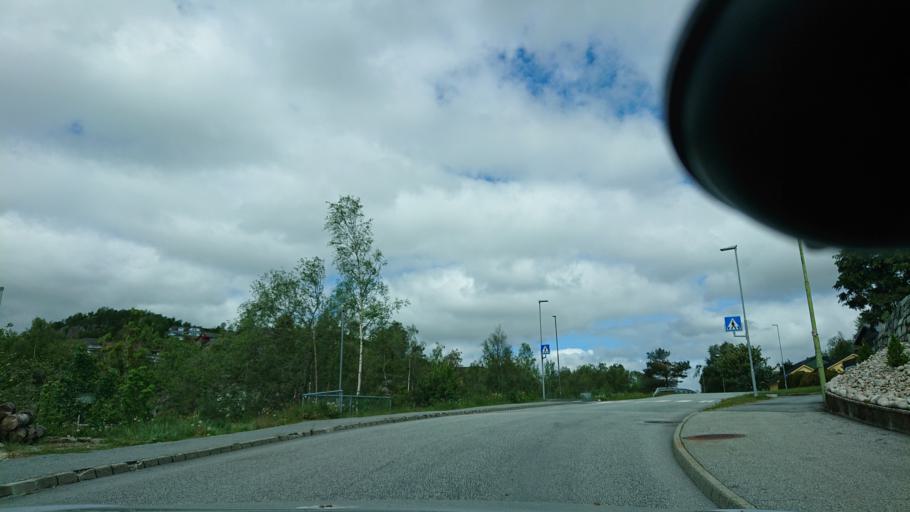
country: NO
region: Rogaland
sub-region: Gjesdal
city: Algard
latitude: 58.7690
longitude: 5.8654
